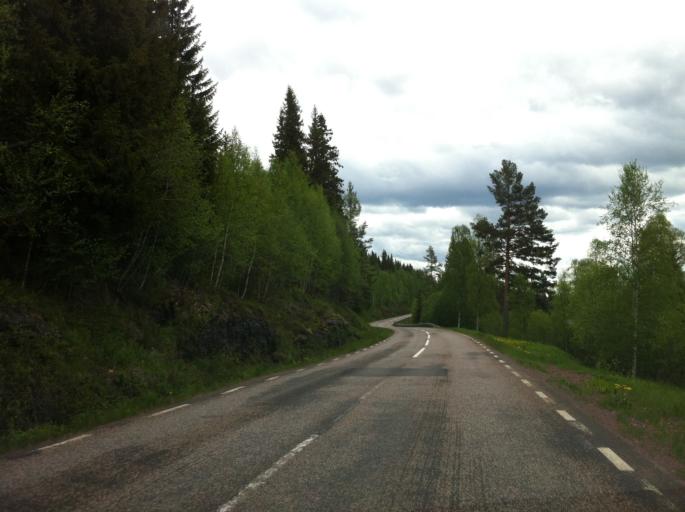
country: SE
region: Dalarna
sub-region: Malung-Saelens kommun
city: Malung
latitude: 61.2213
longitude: 13.2188
